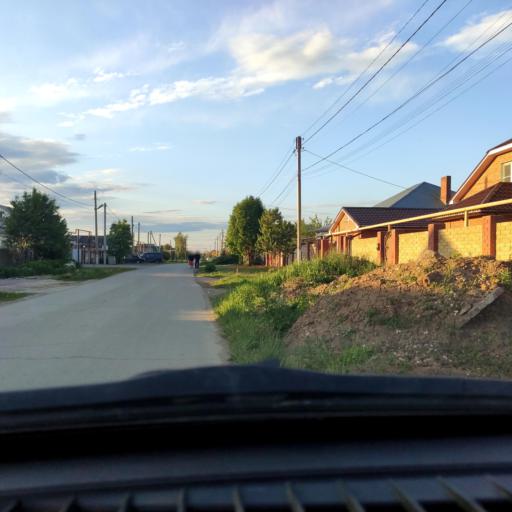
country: RU
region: Samara
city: Tol'yatti
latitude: 53.5625
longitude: 49.4029
